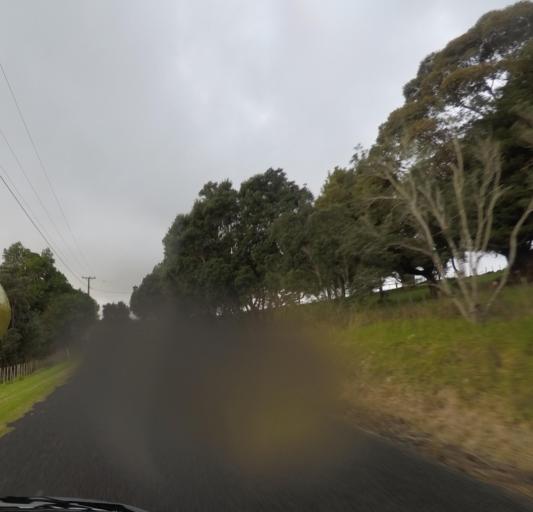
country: NZ
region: Auckland
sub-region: Auckland
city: Warkworth
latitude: -36.3779
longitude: 174.7597
